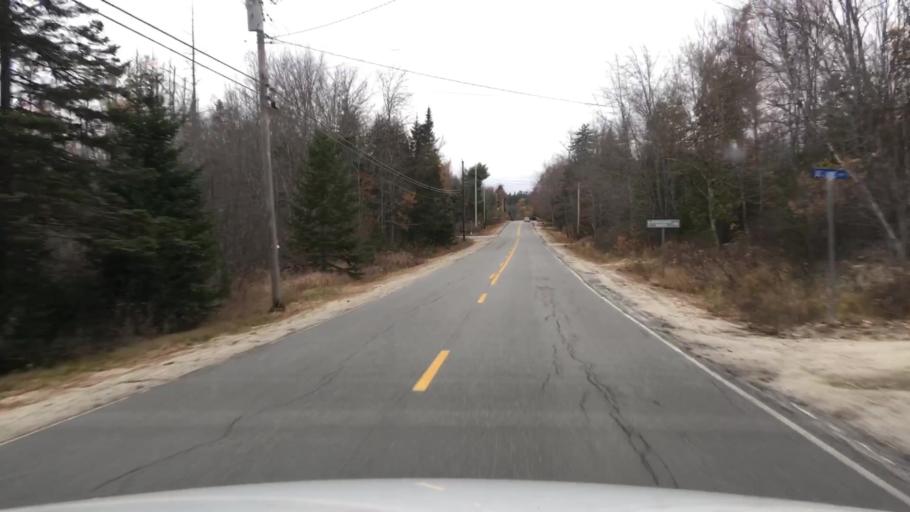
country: US
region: Maine
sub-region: Hancock County
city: Penobscot
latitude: 44.4190
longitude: -68.6154
